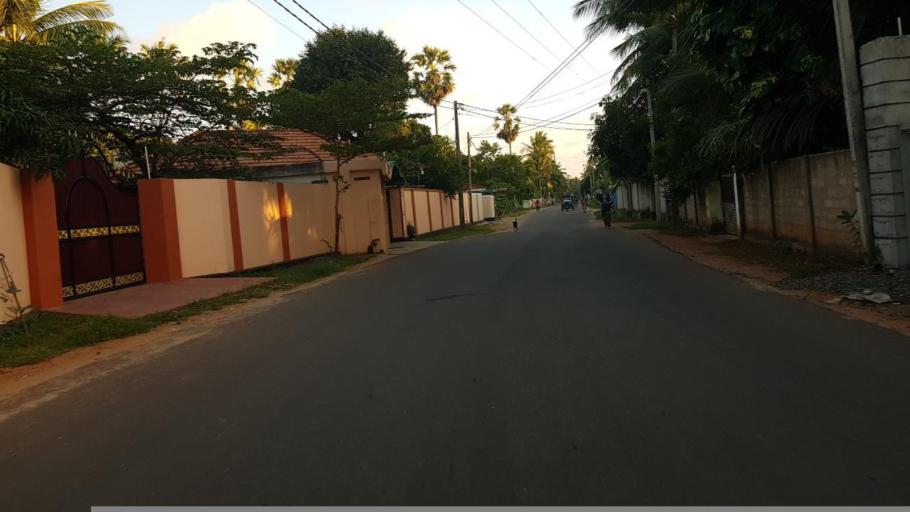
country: LK
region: Northern Province
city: Jaffna
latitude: 9.7162
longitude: 79.9842
